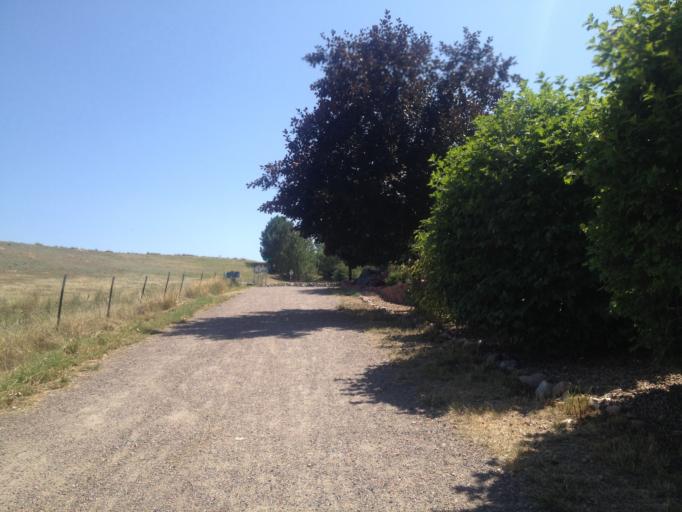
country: US
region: Colorado
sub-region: Boulder County
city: Louisville
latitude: 39.9619
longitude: -105.1422
